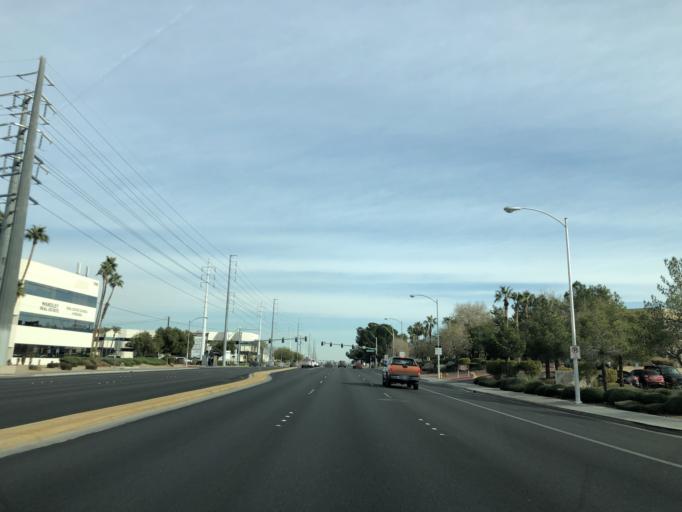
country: US
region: Nevada
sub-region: Clark County
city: Winchester
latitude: 36.1146
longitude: -115.1257
